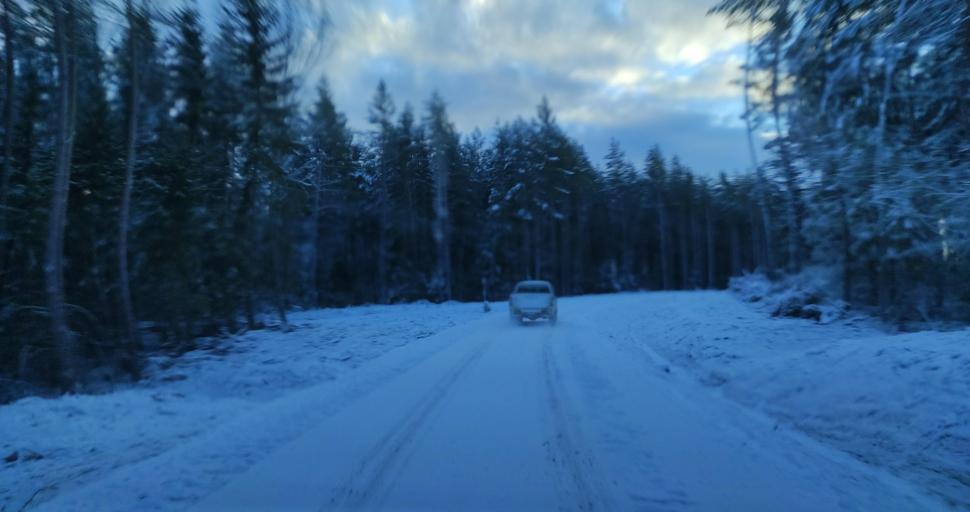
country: LV
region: Skrunda
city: Skrunda
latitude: 56.5906
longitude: 21.9522
